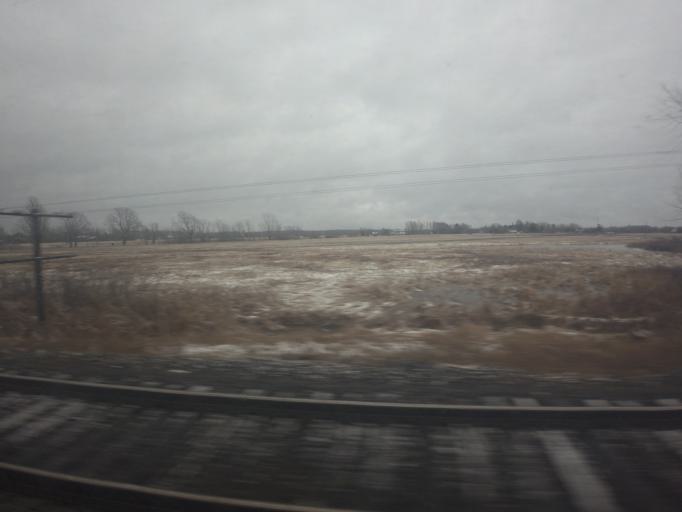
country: CA
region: Ontario
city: Gananoque
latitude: 44.3806
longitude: -76.0724
